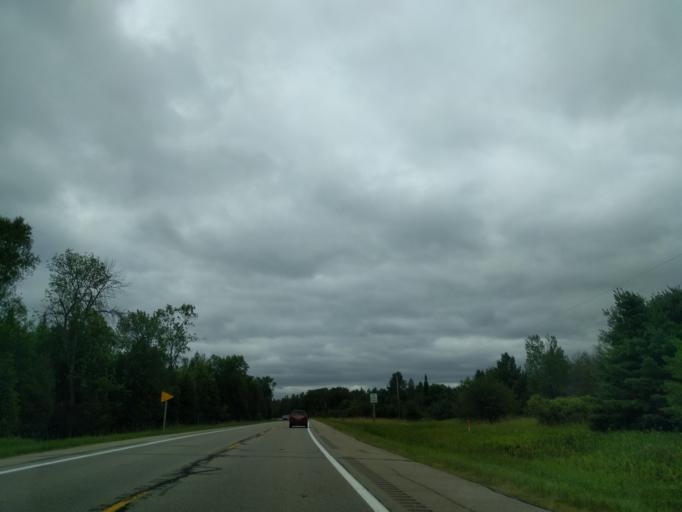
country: US
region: Michigan
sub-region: Delta County
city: Escanaba
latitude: 45.5968
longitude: -87.2297
